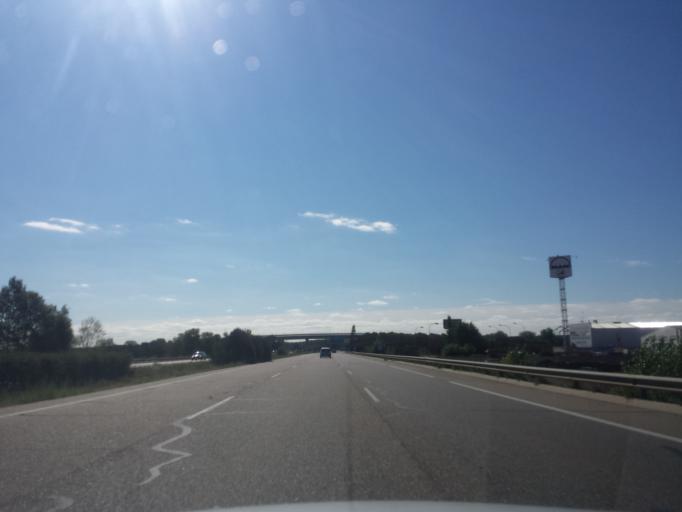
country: ES
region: Castille and Leon
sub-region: Provincia de Zamora
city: Villanueva de Azoague
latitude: 41.9943
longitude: -5.6453
